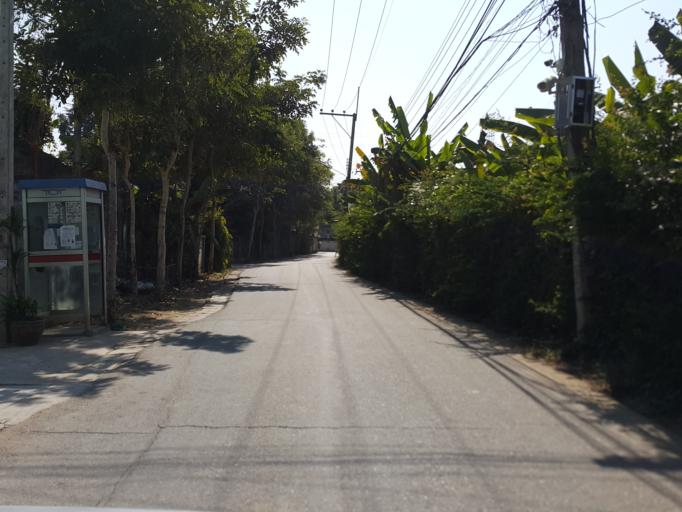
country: TH
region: Chiang Mai
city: Chiang Mai
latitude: 18.8196
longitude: 99.0066
